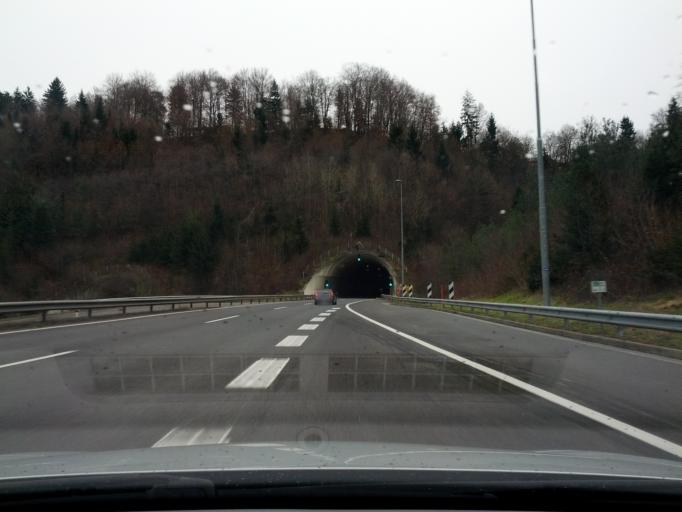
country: SI
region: Skofljica
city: Lavrica
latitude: 46.0111
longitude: 14.5635
